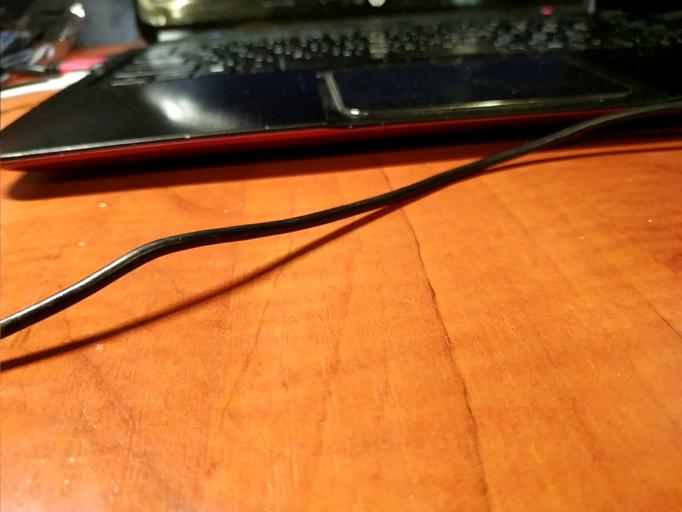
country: RU
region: Tverskaya
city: Rameshki
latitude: 57.2093
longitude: 36.0884
